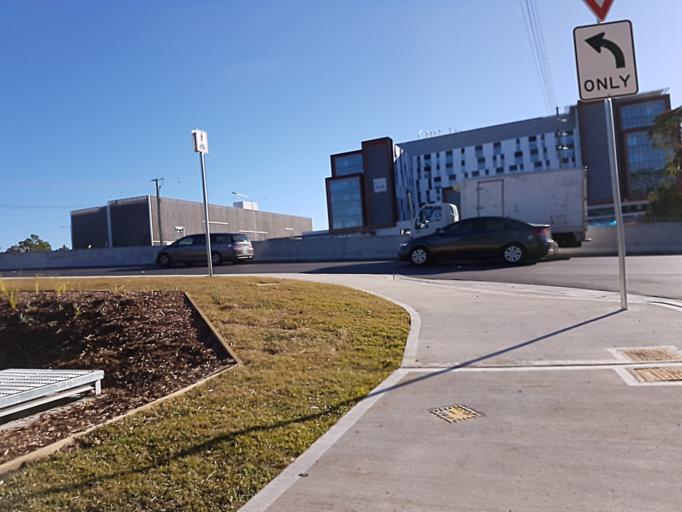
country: AU
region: New South Wales
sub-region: Warringah
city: Allambie Heights
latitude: -33.7525
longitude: 151.2329
